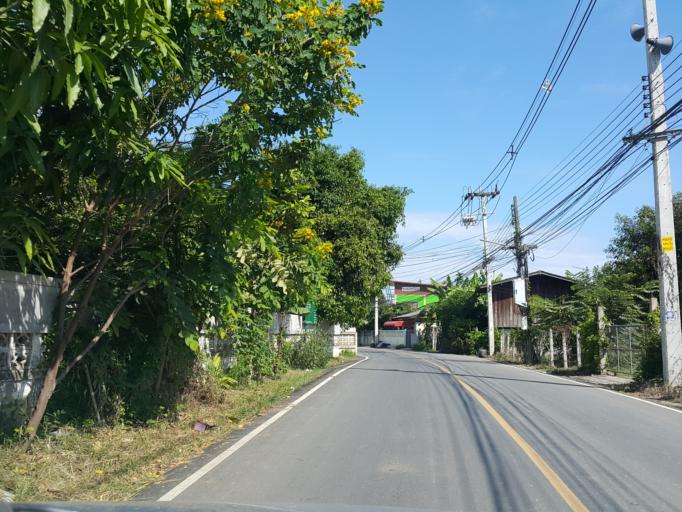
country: TH
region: Chiang Mai
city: San Sai
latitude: 18.7982
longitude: 99.0464
